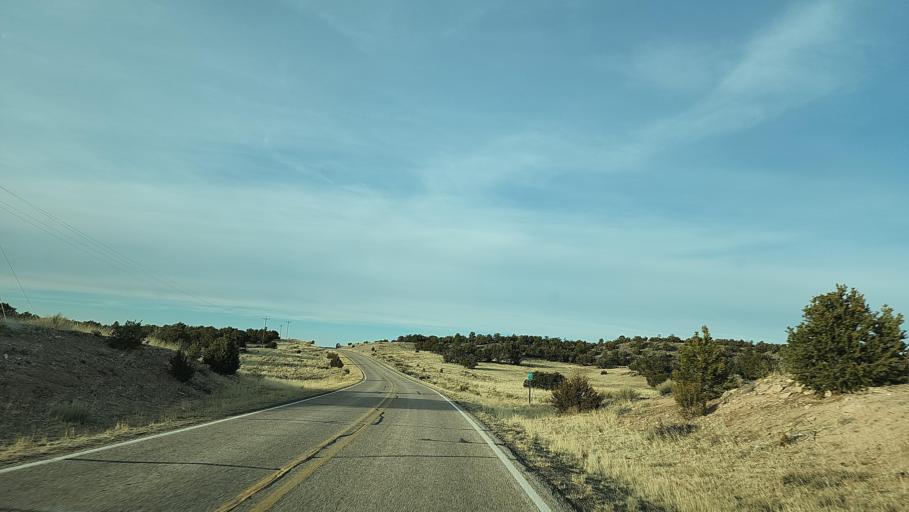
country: US
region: New Mexico
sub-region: McKinley County
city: Black Rock
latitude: 34.4248
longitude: -108.4279
